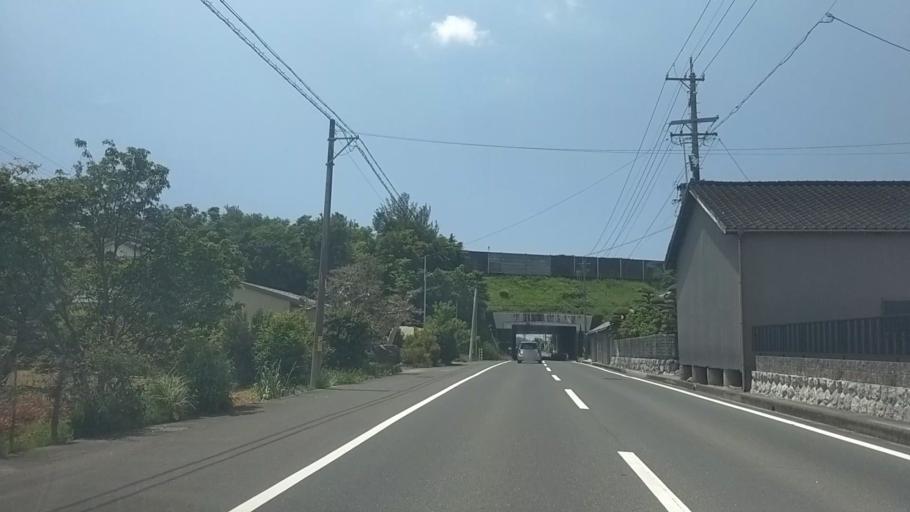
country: JP
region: Shizuoka
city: Hamamatsu
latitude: 34.7667
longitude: 137.6621
